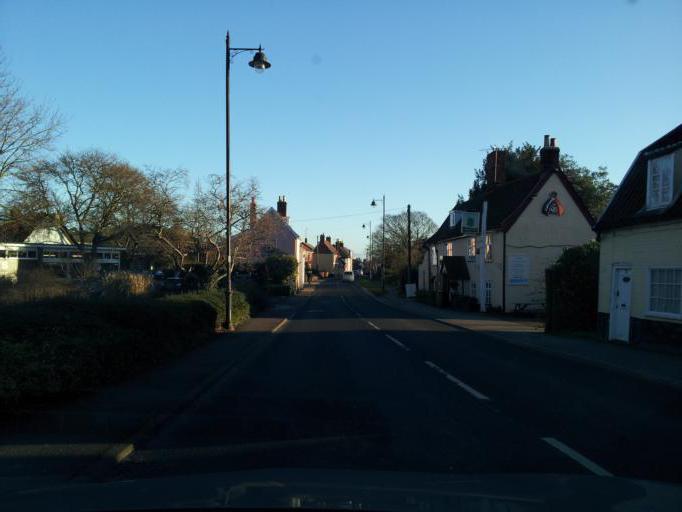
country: GB
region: England
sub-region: Suffolk
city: Woodbridge
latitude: 52.0899
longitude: 1.3097
